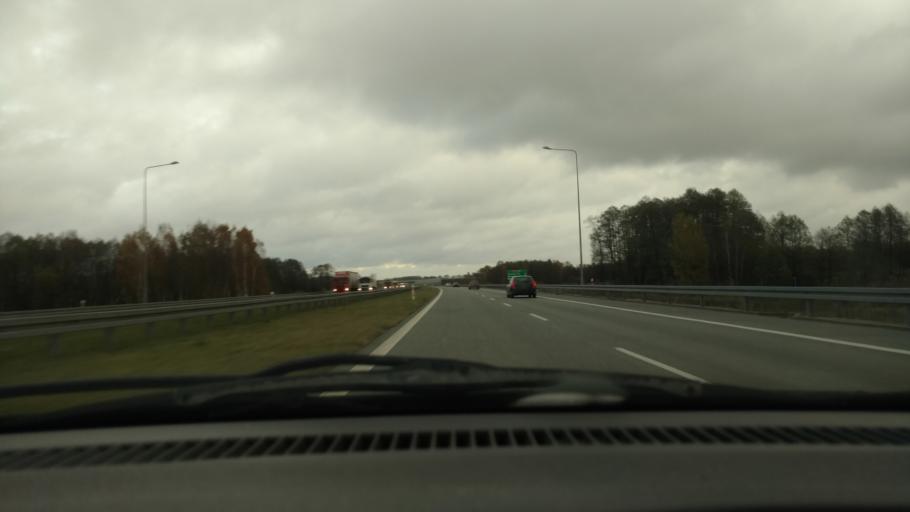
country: PL
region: Lodz Voivodeship
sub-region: Powiat pabianicki
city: Pabianice
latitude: 51.6167
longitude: 19.3740
